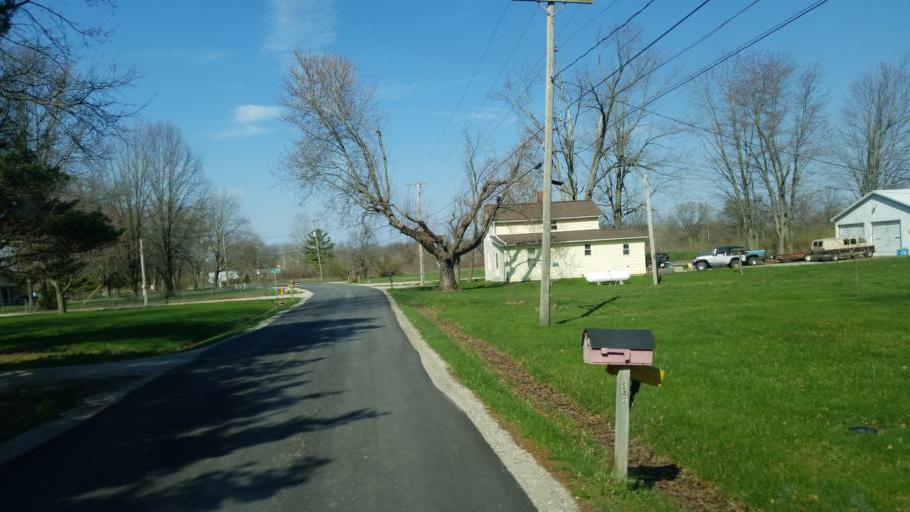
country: US
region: Ohio
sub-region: Delaware County
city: Delaware
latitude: 40.3058
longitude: -83.0426
